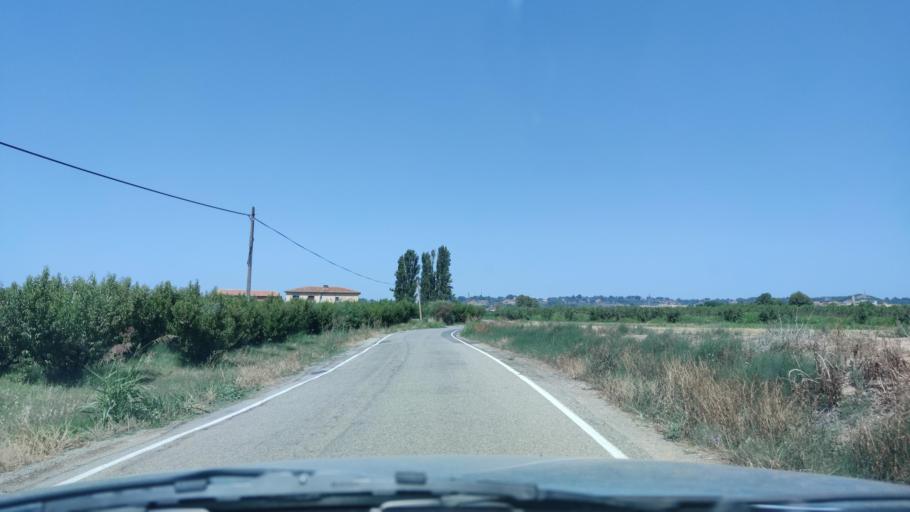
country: ES
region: Catalonia
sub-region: Provincia de Lleida
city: Alpicat
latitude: 41.6575
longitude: 0.5681
